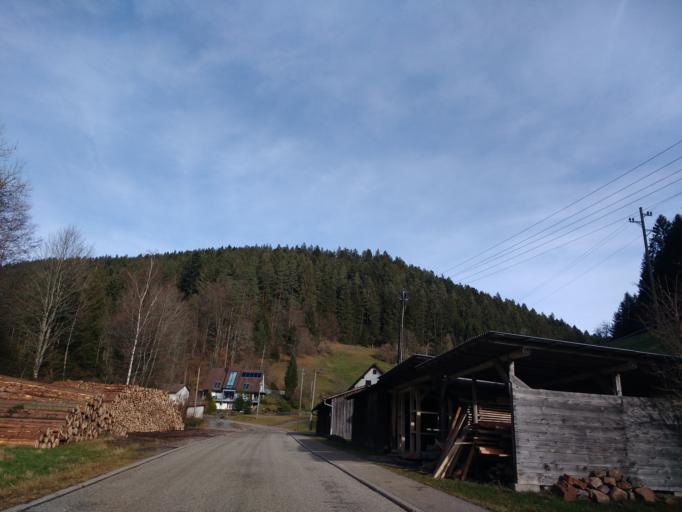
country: DE
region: Baden-Wuerttemberg
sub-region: Karlsruhe Region
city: Bad Rippoldsau-Schapbach
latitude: 48.4550
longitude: 8.2873
